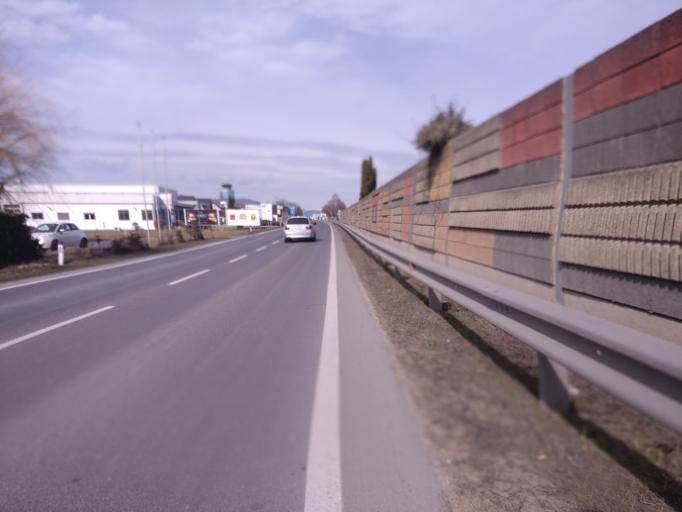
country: AT
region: Styria
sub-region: Politischer Bezirk Graz-Umgebung
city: Feldkirchen bei Graz
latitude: 46.9903
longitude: 15.4497
